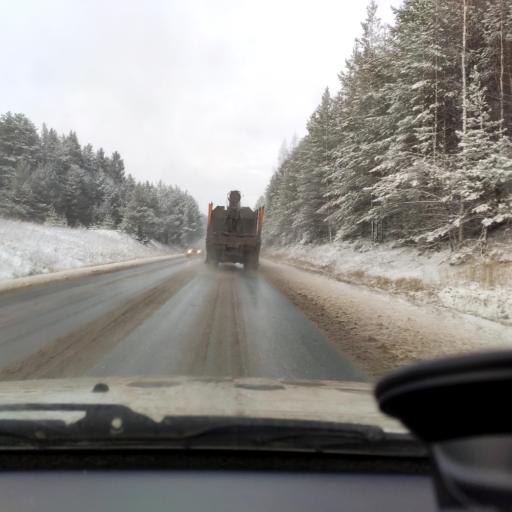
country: RU
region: Perm
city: Nytva
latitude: 57.9692
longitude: 55.3644
